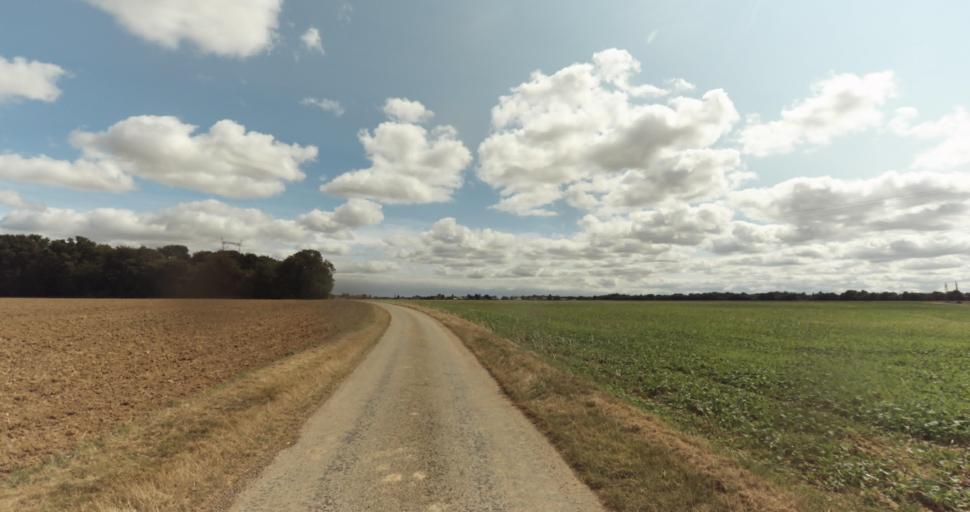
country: FR
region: Haute-Normandie
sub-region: Departement de l'Eure
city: Damville
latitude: 48.8635
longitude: 1.1531
